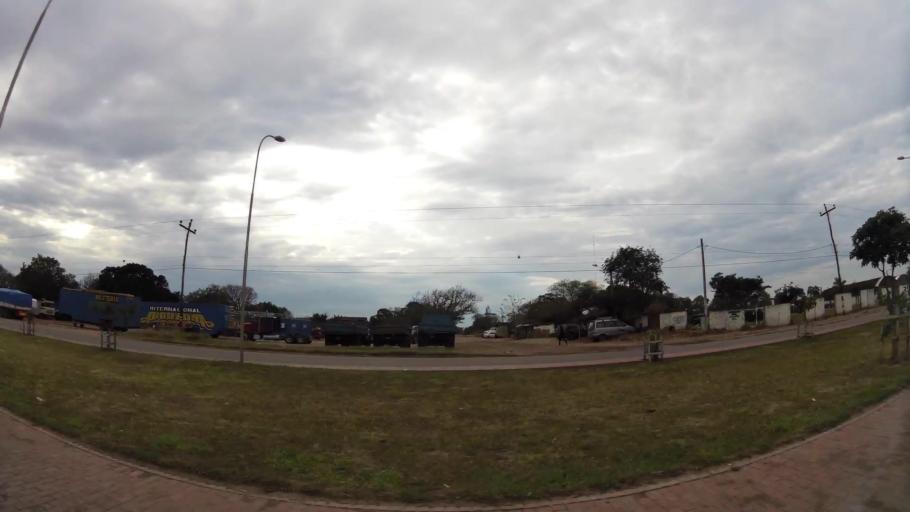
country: BO
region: Santa Cruz
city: Santa Cruz de la Sierra
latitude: -17.7497
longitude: -63.1633
